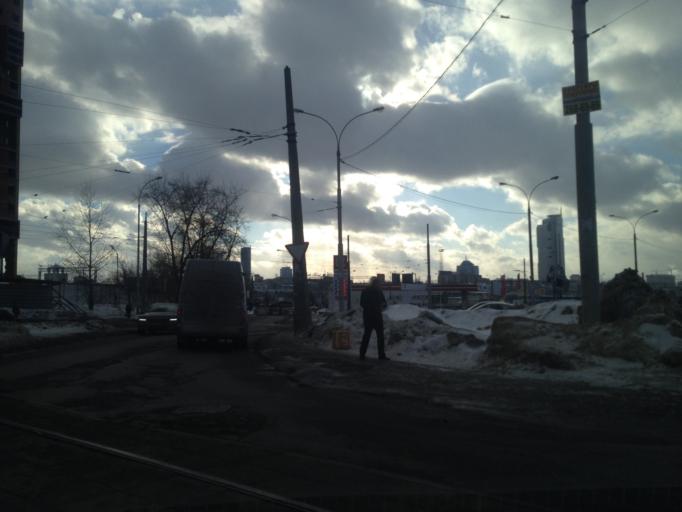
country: RU
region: Sverdlovsk
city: Yekaterinburg
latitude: 56.8614
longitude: 60.6154
